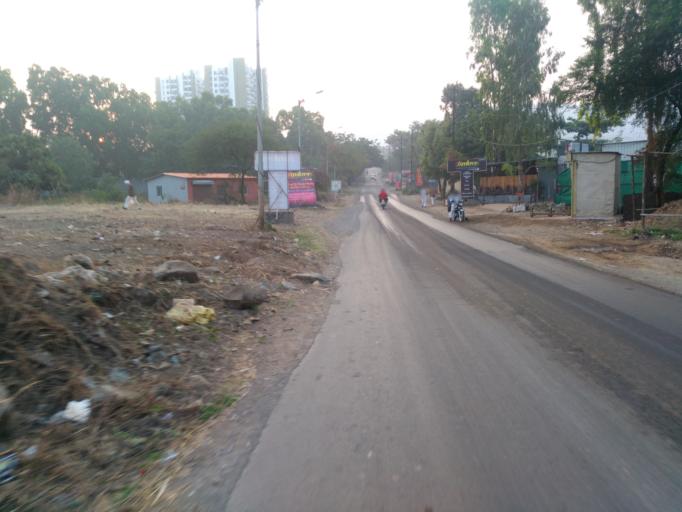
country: IN
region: Maharashtra
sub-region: Pune Division
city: Pune
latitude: 18.4296
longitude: 73.8987
